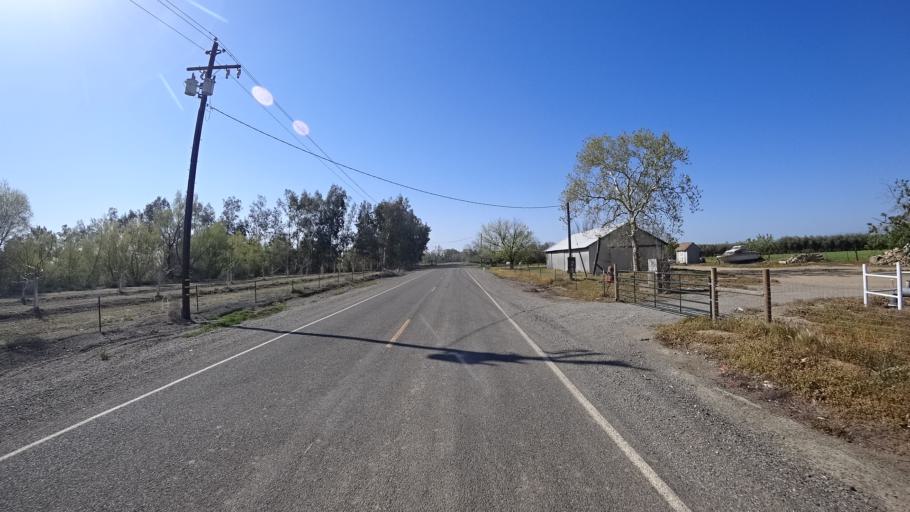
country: US
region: California
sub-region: Glenn County
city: Willows
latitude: 39.5469
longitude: -122.1651
